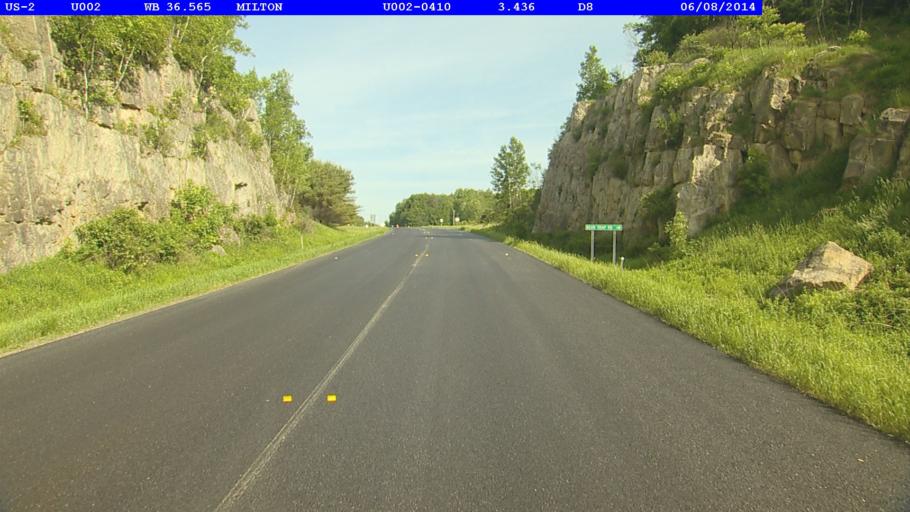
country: US
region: Vermont
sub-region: Chittenden County
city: Colchester
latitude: 44.6070
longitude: -73.2064
